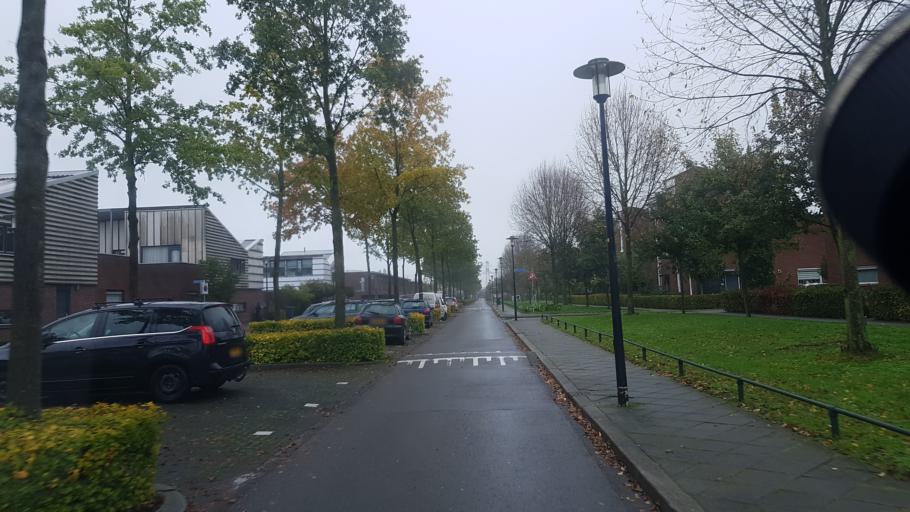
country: NL
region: Gelderland
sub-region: Gemeente Apeldoorn
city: Apeldoorn
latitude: 52.2184
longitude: 6.0111
